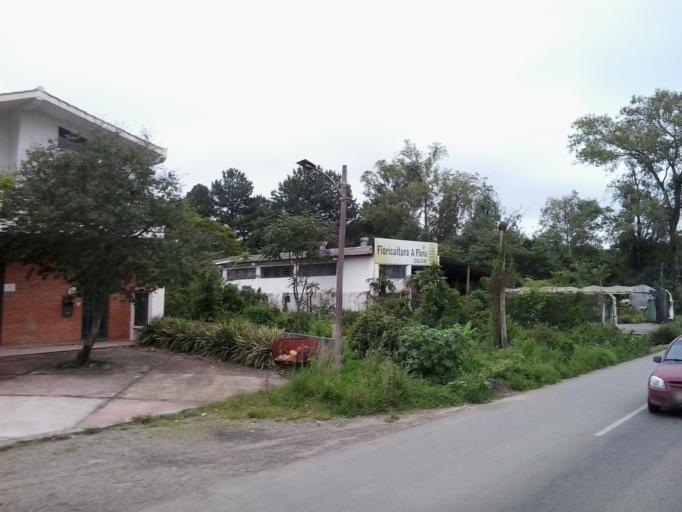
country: BR
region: Rio Grande do Sul
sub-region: Santa Maria
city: Santa Maria
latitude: -29.6943
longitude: -53.7601
